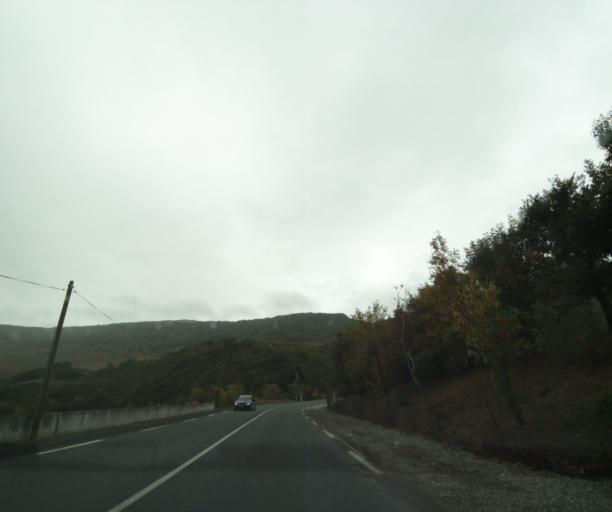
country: FR
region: Midi-Pyrenees
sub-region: Departement de l'Aveyron
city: Millau
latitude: 44.0919
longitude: 3.0906
